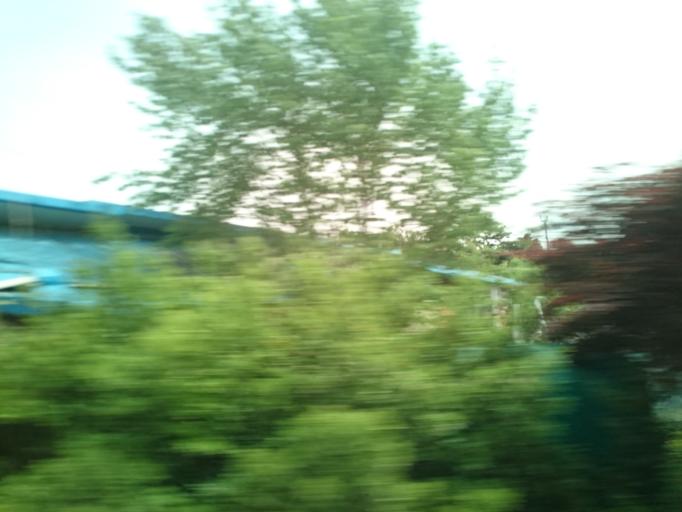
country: KR
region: Jeollabuk-do
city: Wanju
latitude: 35.8949
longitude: 127.1926
